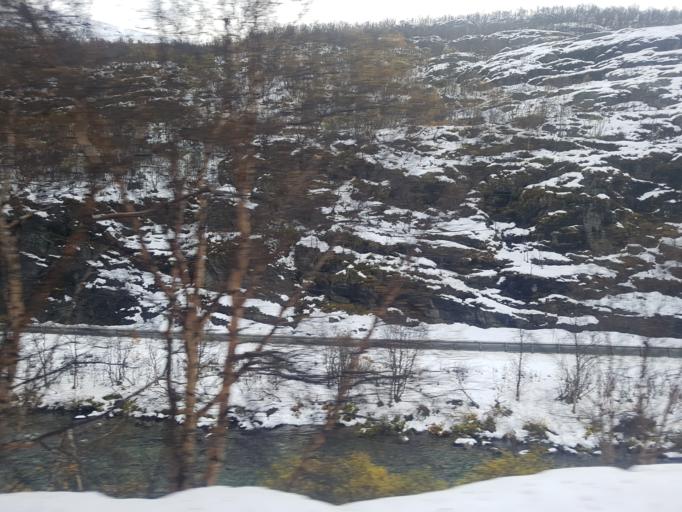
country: NO
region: Sor-Trondelag
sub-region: Oppdal
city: Oppdal
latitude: 62.3332
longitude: 9.6217
